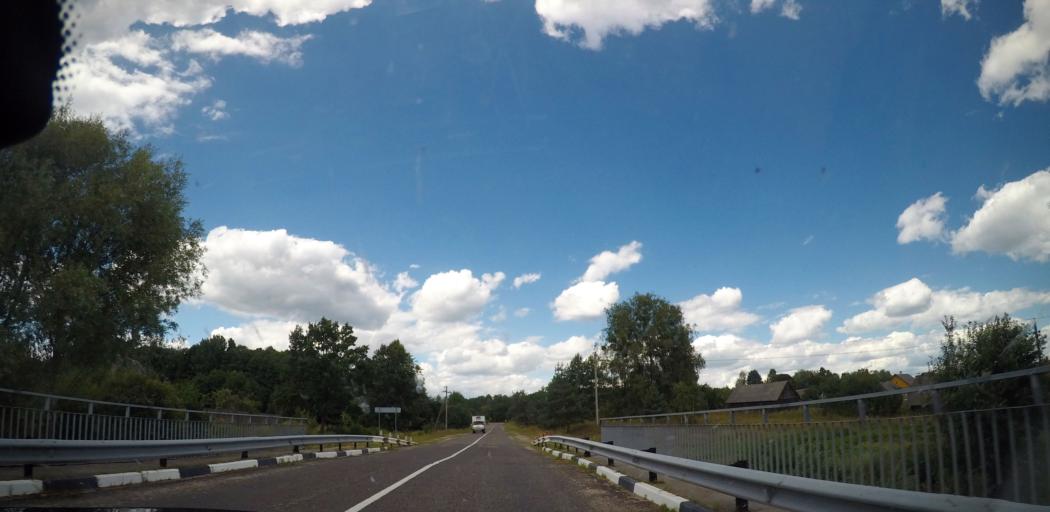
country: BY
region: Grodnenskaya
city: Skidal'
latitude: 53.8202
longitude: 24.2431
